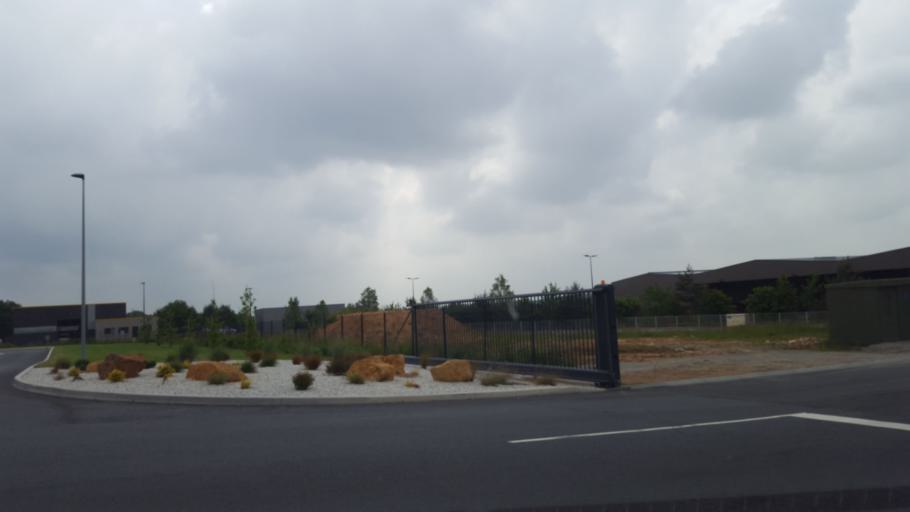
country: FR
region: Brittany
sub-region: Departement d'Ille-et-Vilaine
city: Grand-Fougeray
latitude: 47.7482
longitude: -1.7212
